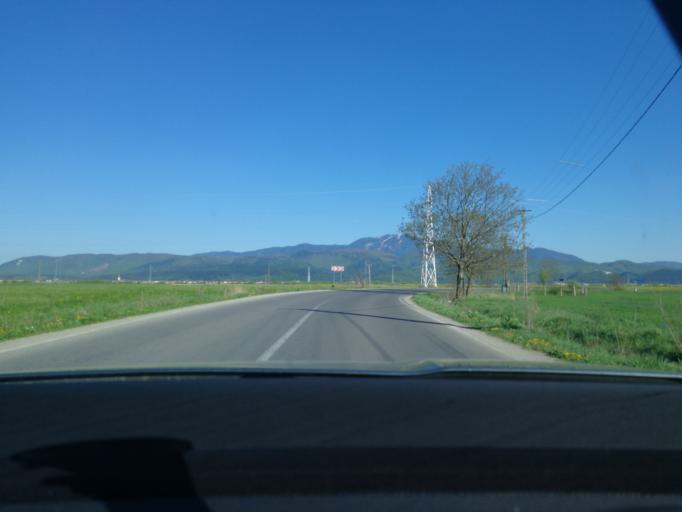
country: RO
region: Brasov
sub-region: Comuna Vulcan
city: Vulcan
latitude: 45.6282
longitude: 25.4256
